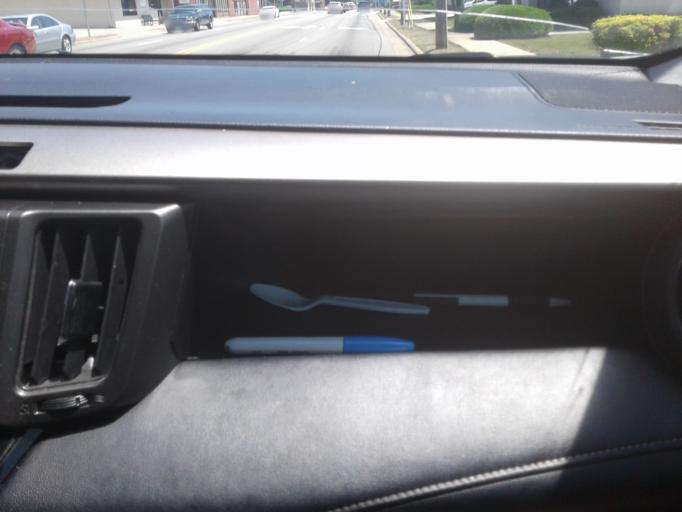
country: US
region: North Carolina
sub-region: Harnett County
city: Dunn
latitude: 35.3074
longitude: -78.6111
